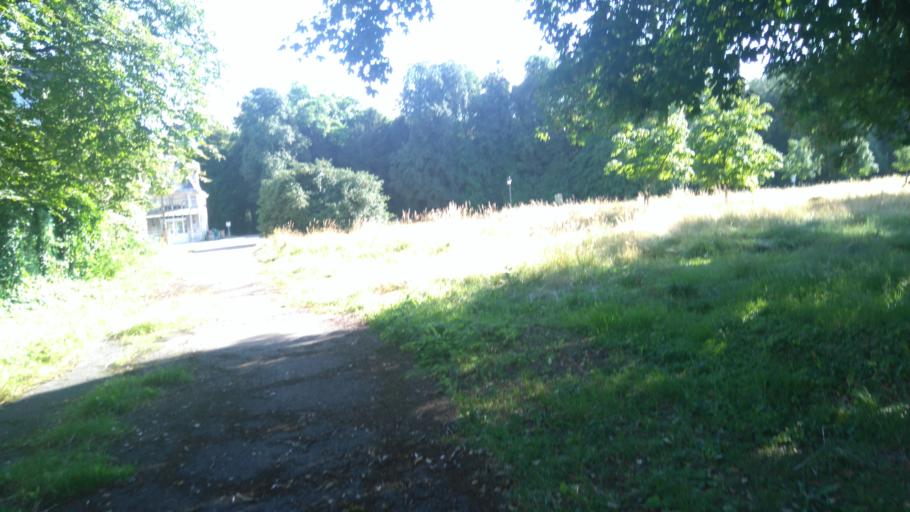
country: FR
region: Picardie
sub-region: Departement de l'Oise
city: Saint-Maximin
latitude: 49.2366
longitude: 2.4594
